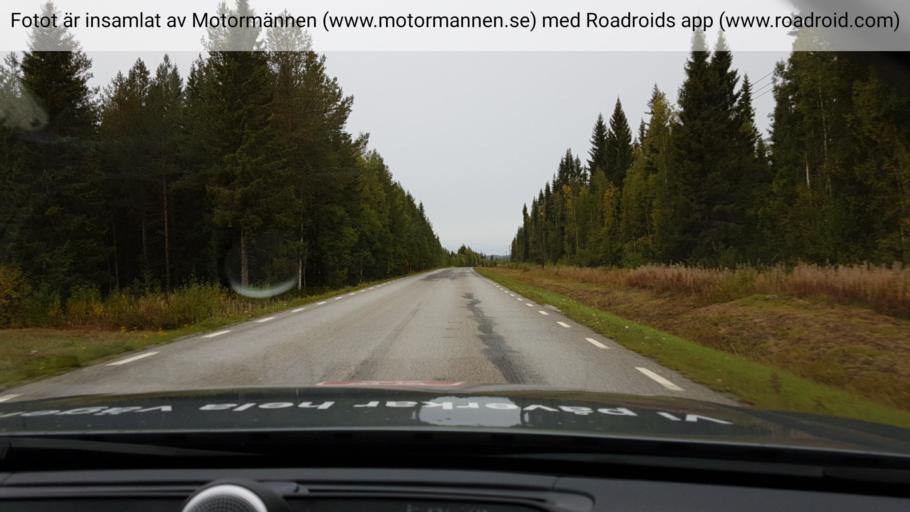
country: SE
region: Jaemtland
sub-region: Stroemsunds Kommun
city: Stroemsund
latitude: 63.9304
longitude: 15.5015
